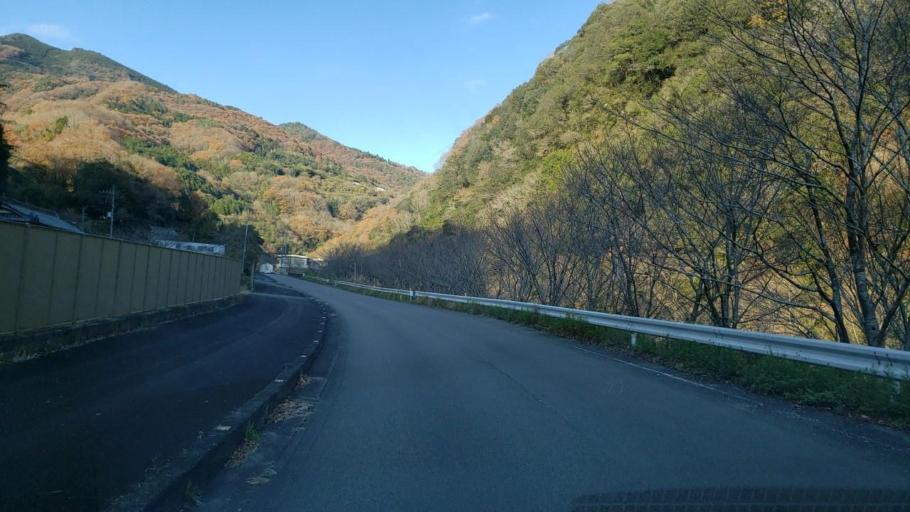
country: JP
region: Tokushima
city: Wakimachi
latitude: 34.0927
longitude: 134.0685
